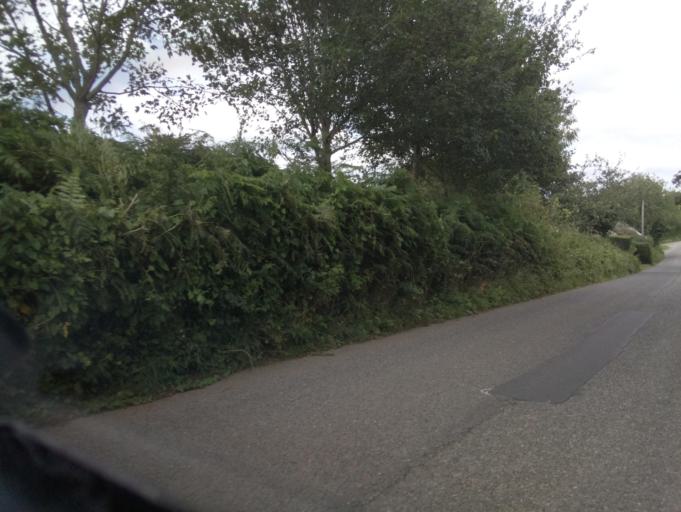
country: GB
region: England
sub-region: Devon
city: South Brent
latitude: 50.3955
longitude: -3.8393
